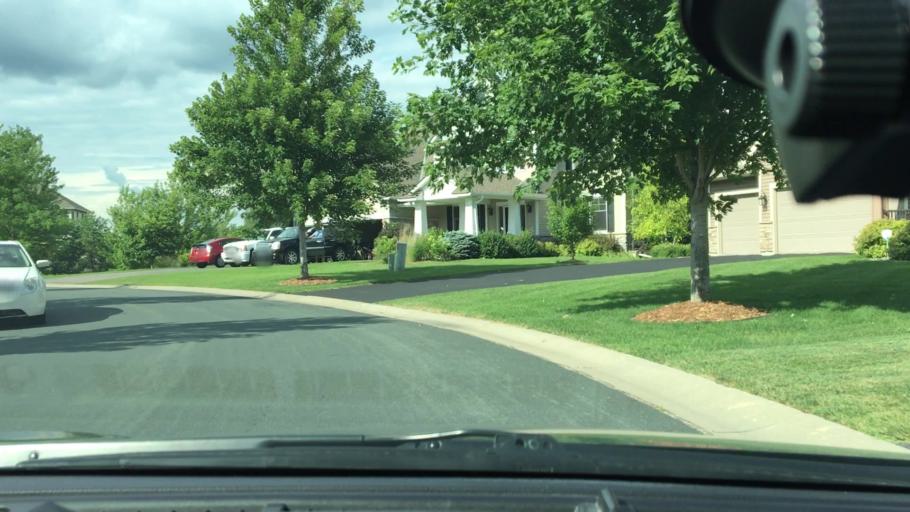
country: US
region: Minnesota
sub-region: Carver County
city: Victoria
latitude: 44.8582
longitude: -93.6805
